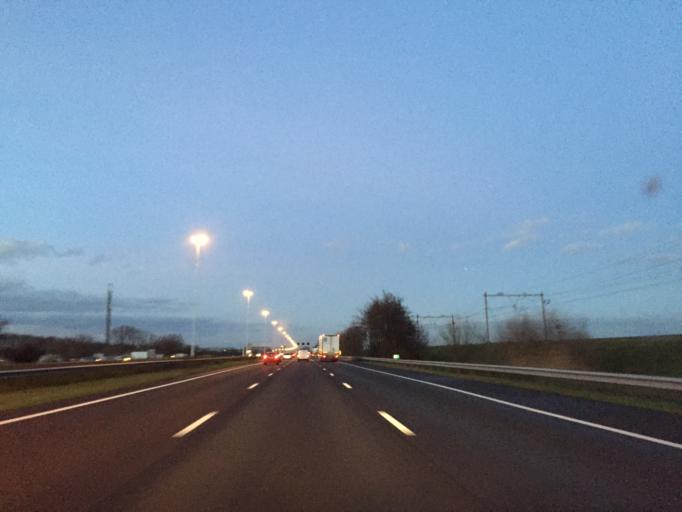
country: NL
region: South Holland
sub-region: Gemeente Zwijndrecht
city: Zwijndrecht
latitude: 51.7422
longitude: 4.6371
